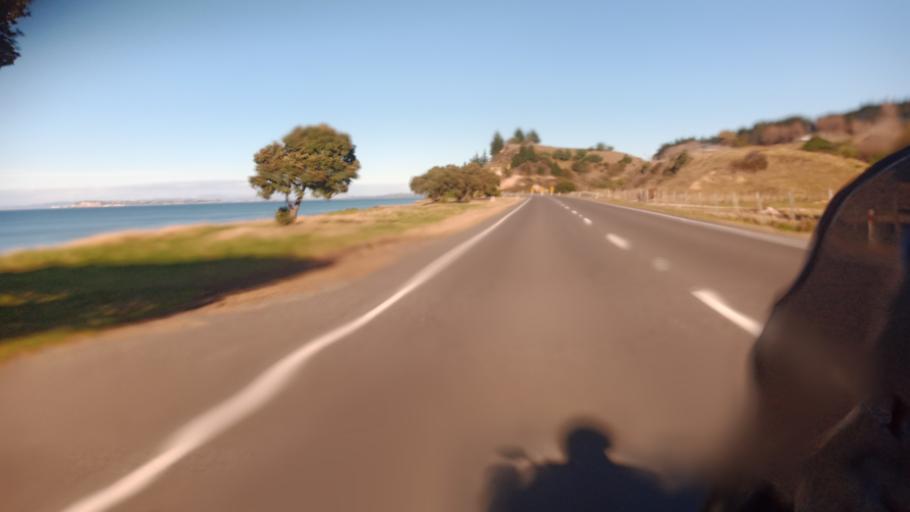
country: NZ
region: Hawke's Bay
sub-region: Napier City
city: Napier
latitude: -39.3599
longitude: 176.9040
